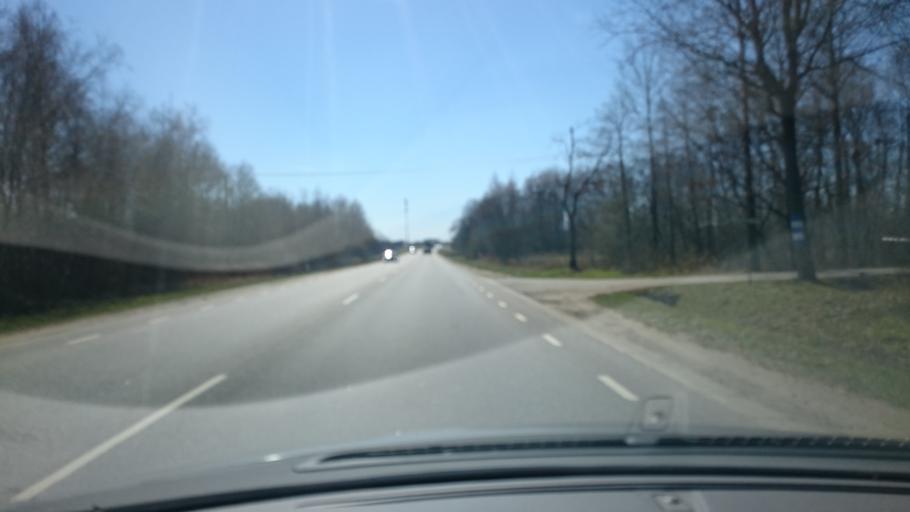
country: EE
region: Harju
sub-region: Rae vald
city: Jueri
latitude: 59.3676
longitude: 24.9050
